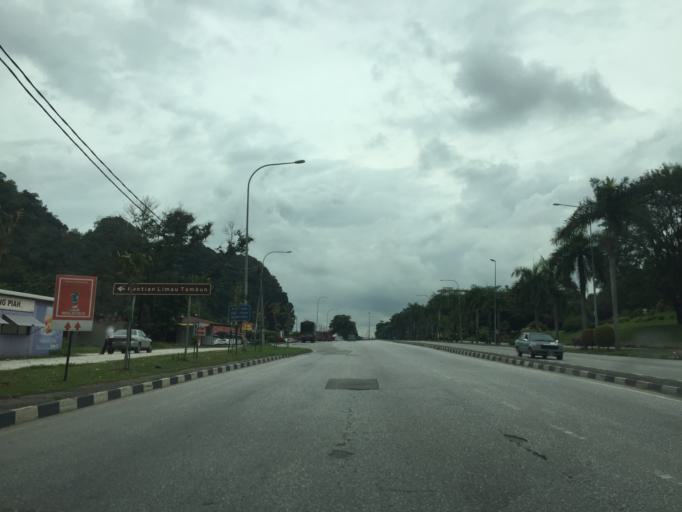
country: MY
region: Perak
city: Ipoh
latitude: 4.5659
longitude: 101.1134
